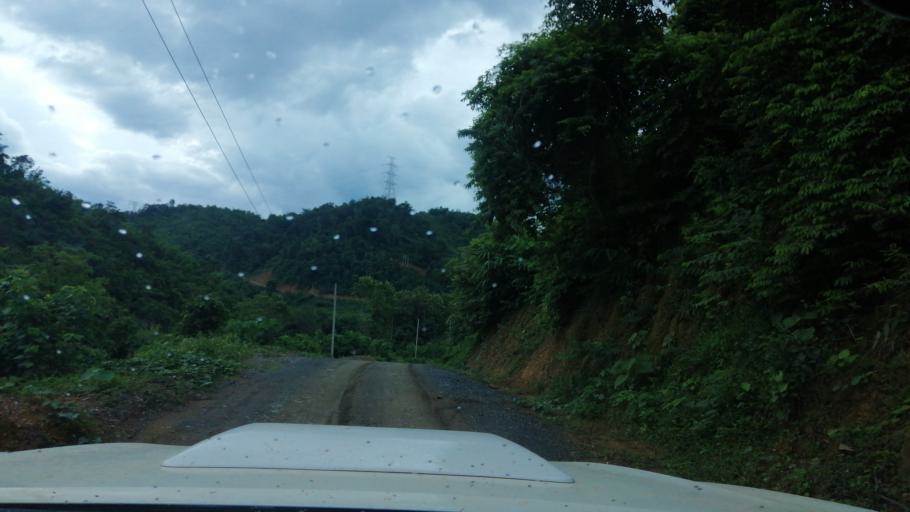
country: LA
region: Xiagnabouli
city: Sainyabuli
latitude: 19.1854
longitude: 101.7922
